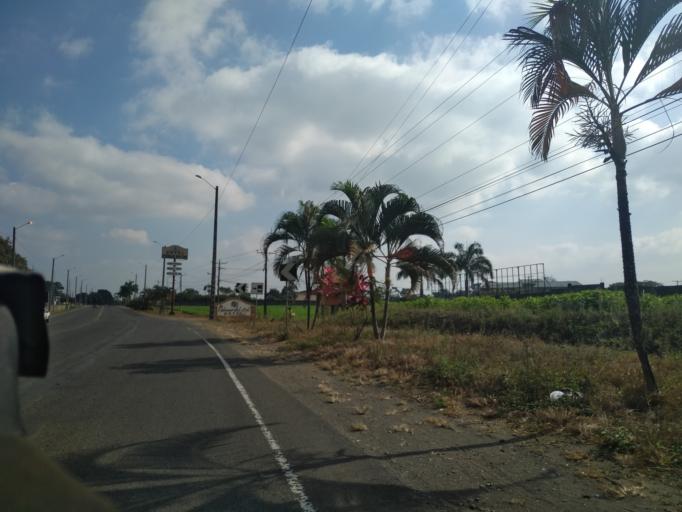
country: EC
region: Los Rios
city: Quevedo
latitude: -1.0681
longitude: -79.4948
